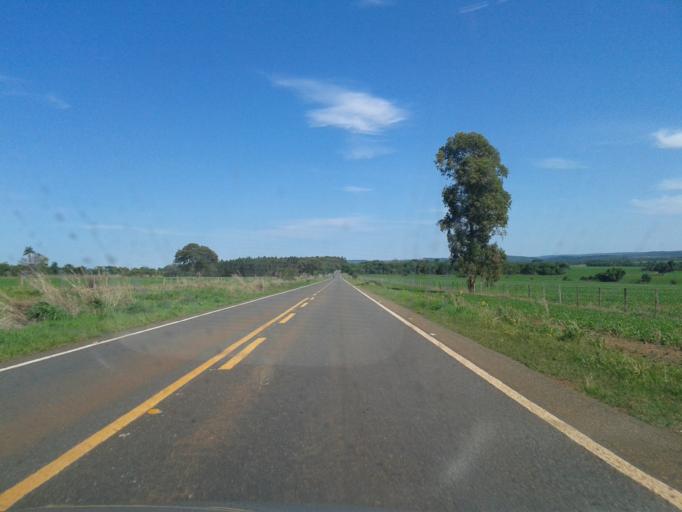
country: BR
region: Goias
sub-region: Piracanjuba
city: Piracanjuba
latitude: -17.3382
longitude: -48.7948
